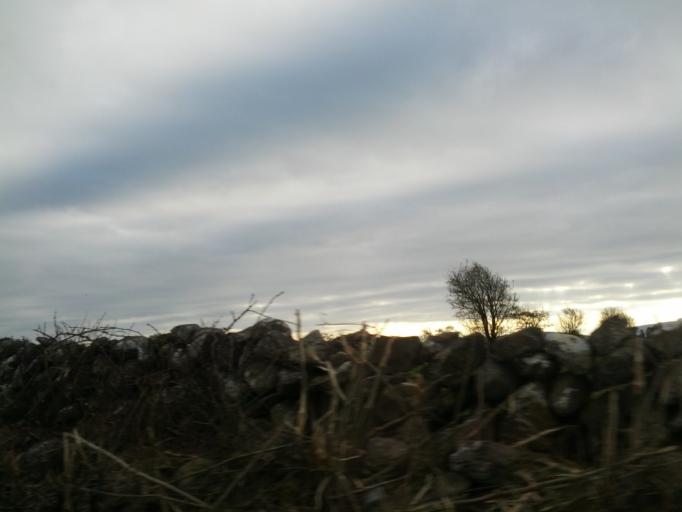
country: IE
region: Connaught
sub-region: County Galway
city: Gort
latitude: 53.1586
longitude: -8.8722
